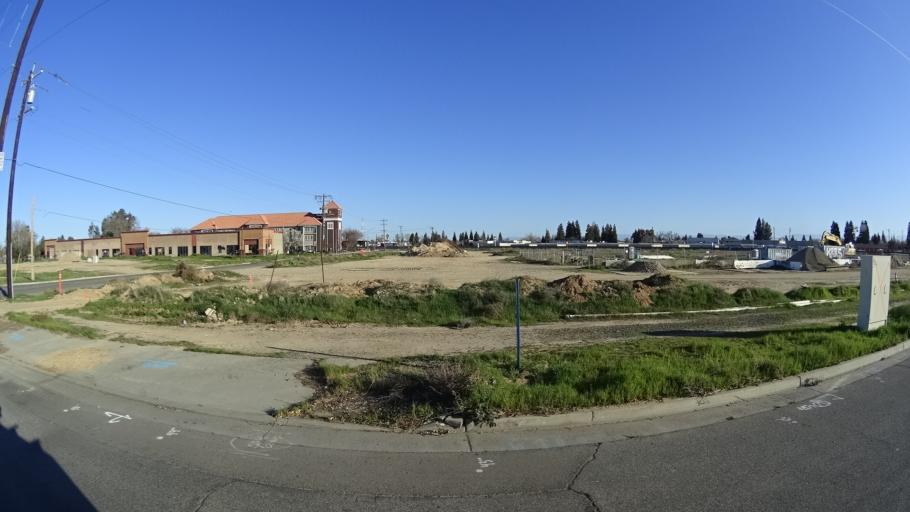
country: US
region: California
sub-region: Fresno County
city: West Park
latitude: 36.8082
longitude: -119.8802
